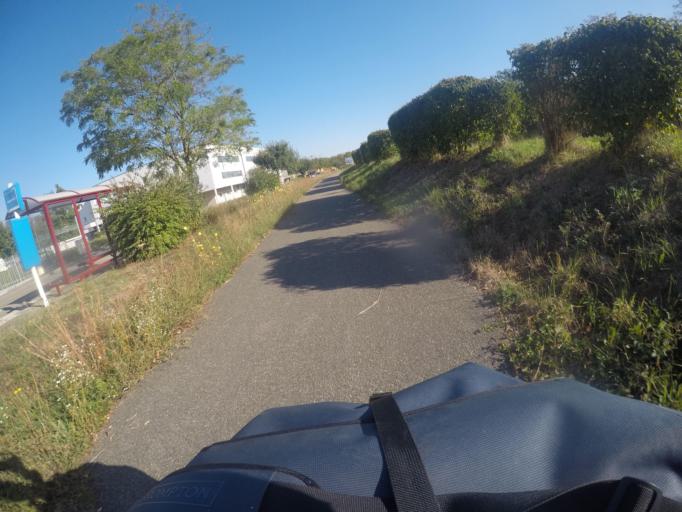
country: FR
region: Alsace
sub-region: Departement du Haut-Rhin
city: Kembs
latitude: 47.6722
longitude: 7.4982
